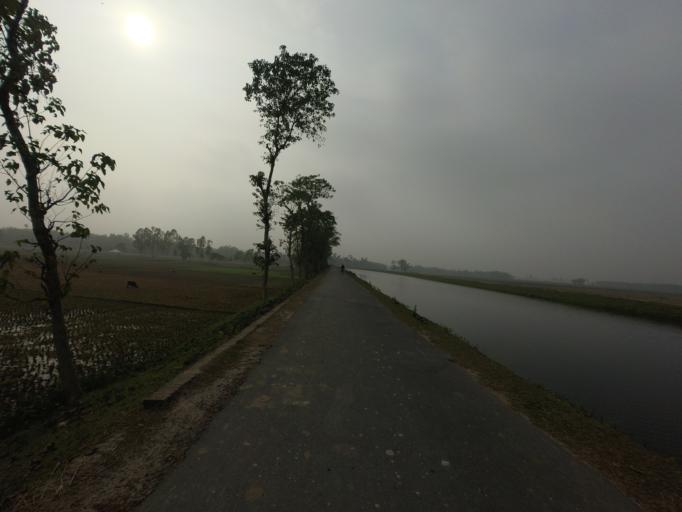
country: BD
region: Rajshahi
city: Saidpur
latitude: 25.9763
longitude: 88.9159
